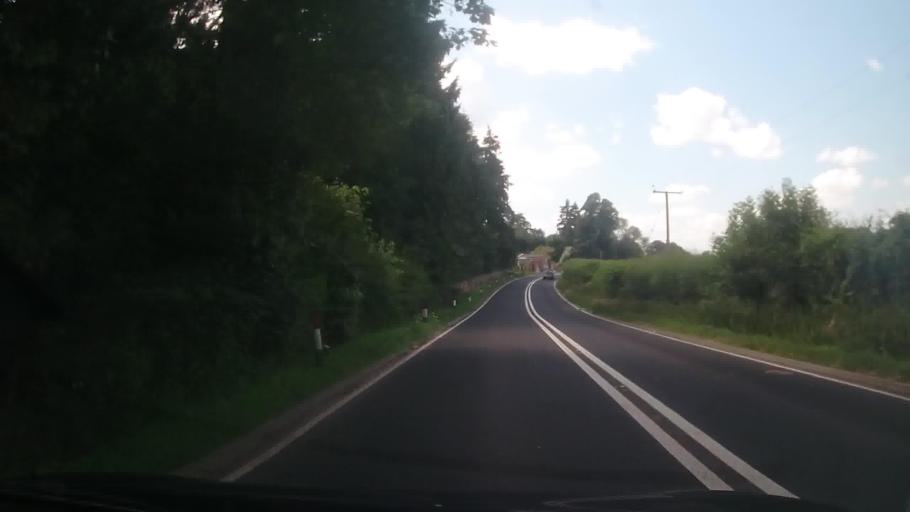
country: GB
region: England
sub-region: Herefordshire
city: Ocle Pychard
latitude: 52.0649
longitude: -2.5694
